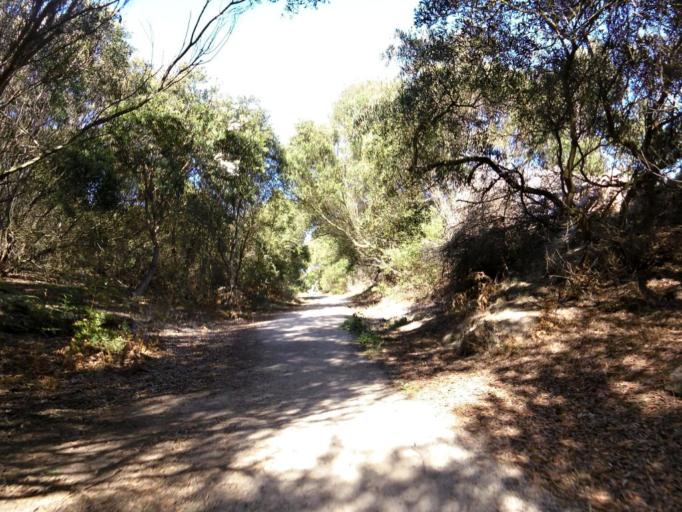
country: AU
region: Victoria
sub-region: Bass Coast
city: North Wonthaggi
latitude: -38.6134
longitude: 145.6009
